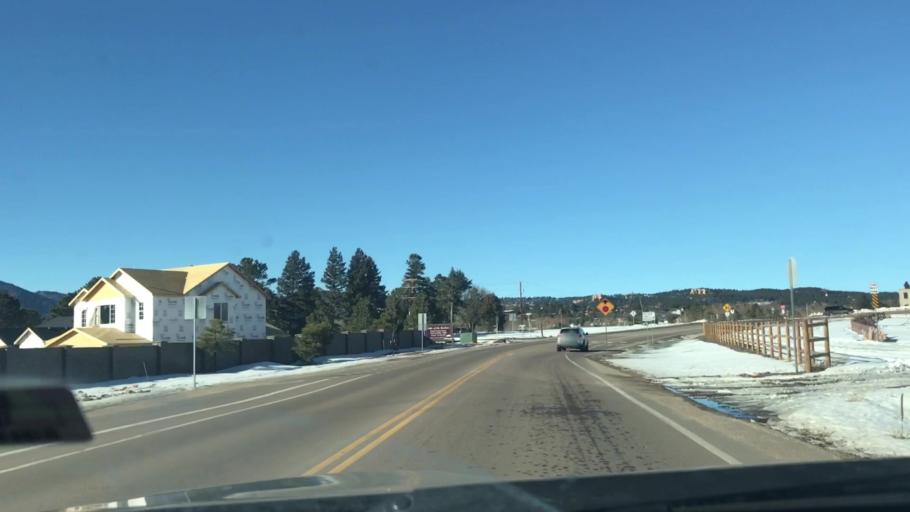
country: US
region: Colorado
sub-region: El Paso County
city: Monument
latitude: 39.0899
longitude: -104.8754
